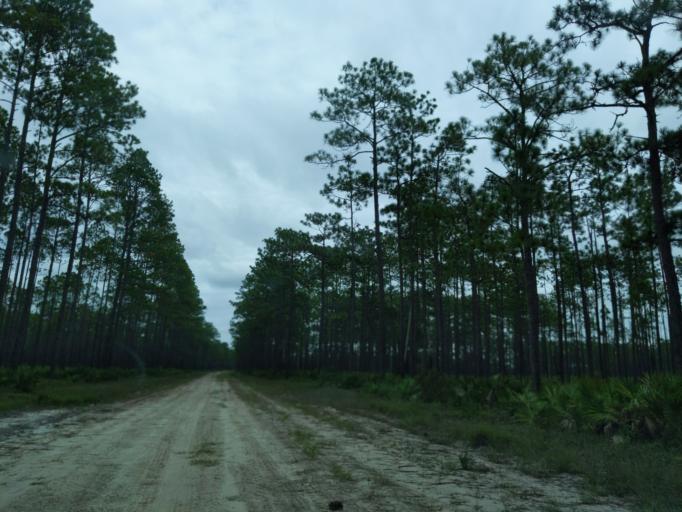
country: US
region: Florida
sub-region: Gadsden County
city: Midway
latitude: 30.3659
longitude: -84.4741
